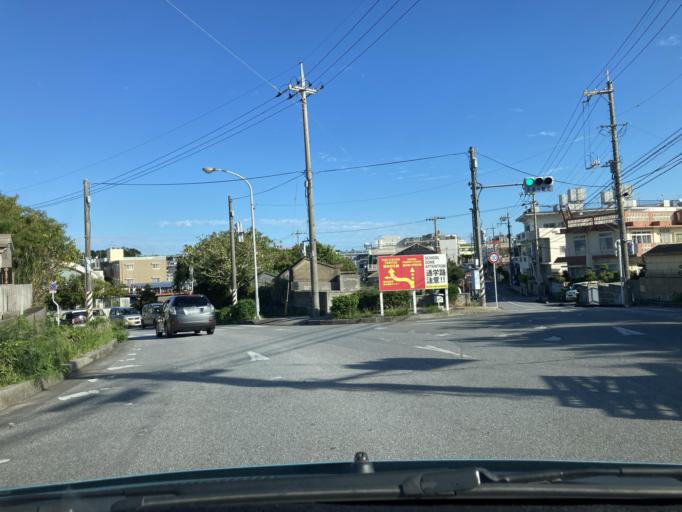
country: JP
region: Okinawa
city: Chatan
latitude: 26.3610
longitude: 127.7493
